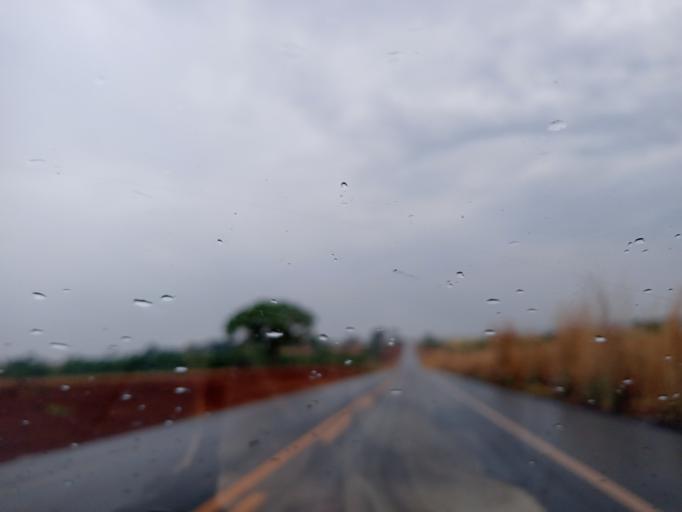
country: BR
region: Minas Gerais
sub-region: Ituiutaba
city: Ituiutaba
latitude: -19.1740
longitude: -49.5183
